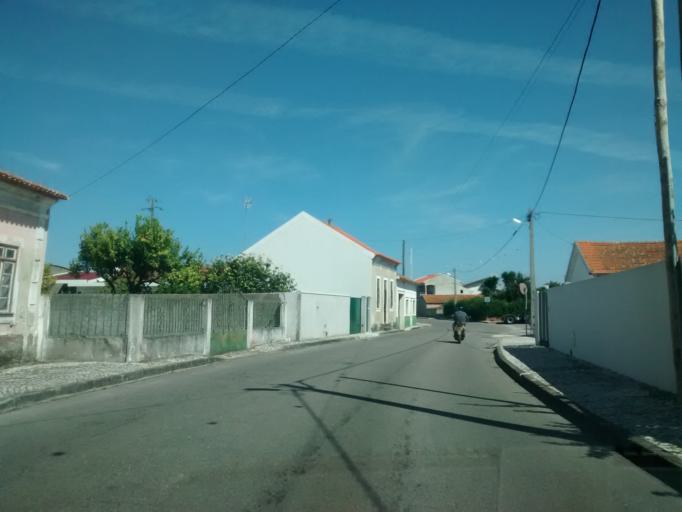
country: PT
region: Coimbra
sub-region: Mira
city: Mira
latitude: 40.4344
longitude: -8.7126
